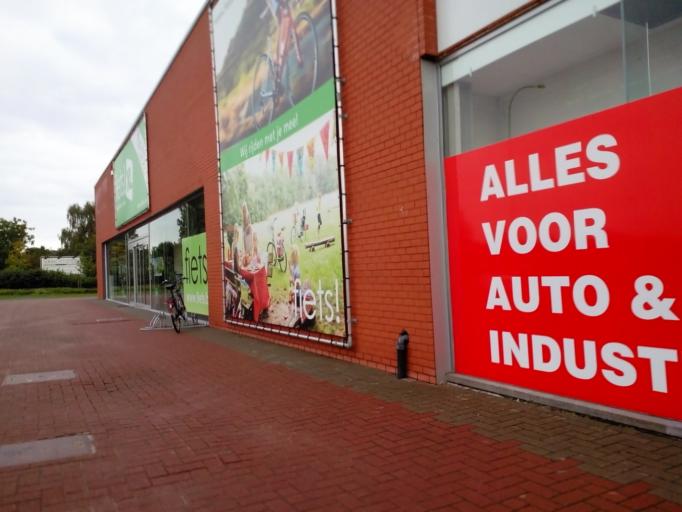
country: BE
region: Flanders
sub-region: Provincie Vlaams-Brabant
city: Leuven
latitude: 50.8918
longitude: 4.6909
